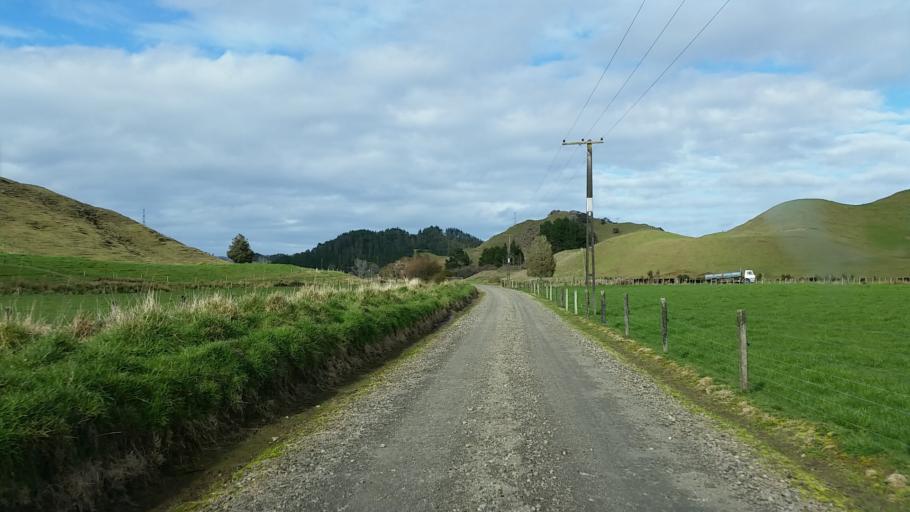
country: NZ
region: Taranaki
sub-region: South Taranaki District
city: Eltham
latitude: -39.2241
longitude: 174.5630
